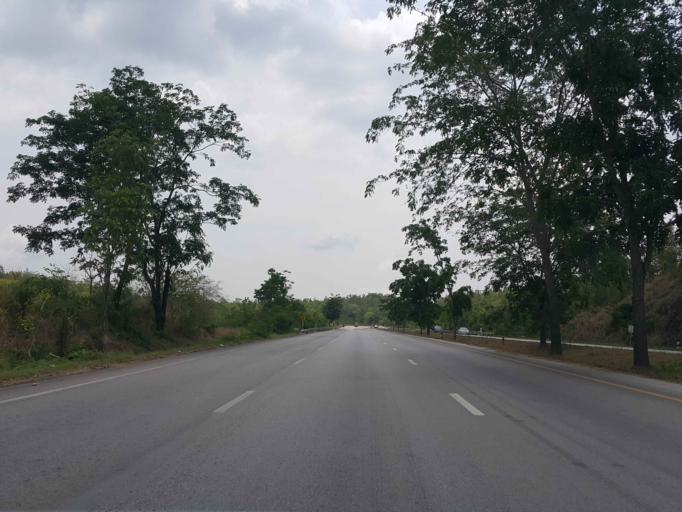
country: TH
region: Lampang
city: Soem Ngam
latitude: 18.0496
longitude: 99.3852
